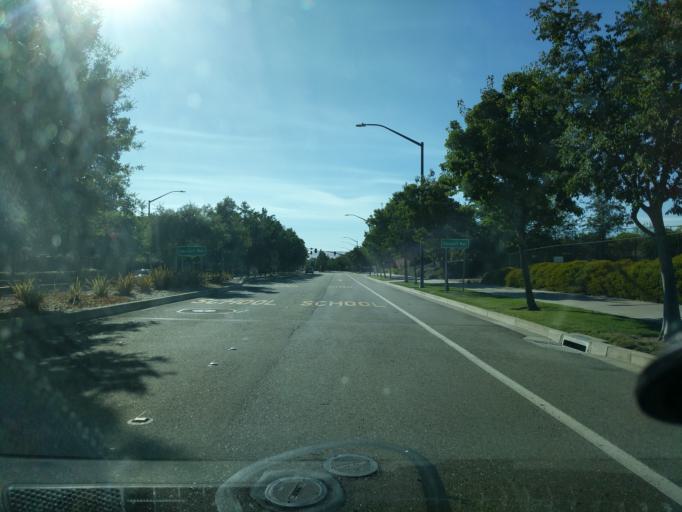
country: US
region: California
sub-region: Contra Costa County
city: Blackhawk
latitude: 37.7625
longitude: -121.8928
